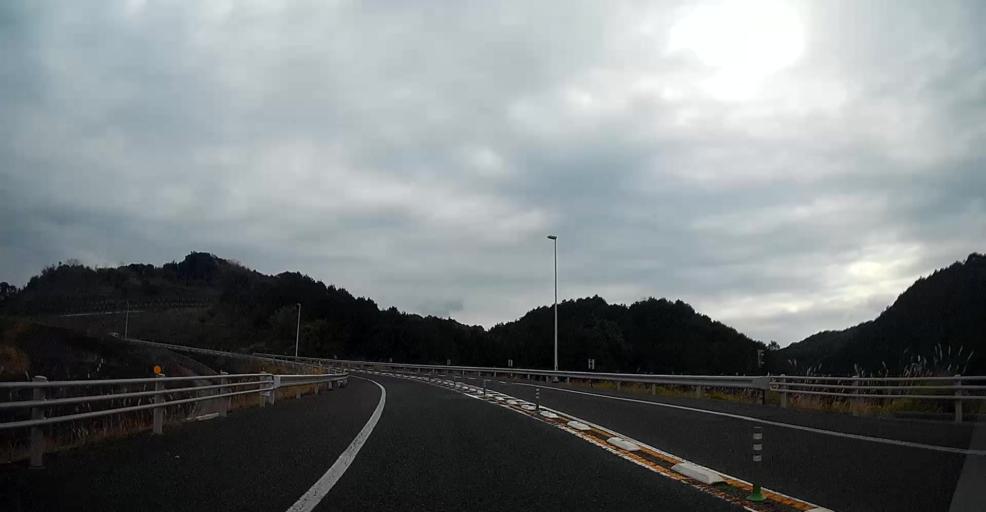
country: JP
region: Kumamoto
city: Hondo
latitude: 32.5017
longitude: 130.3055
